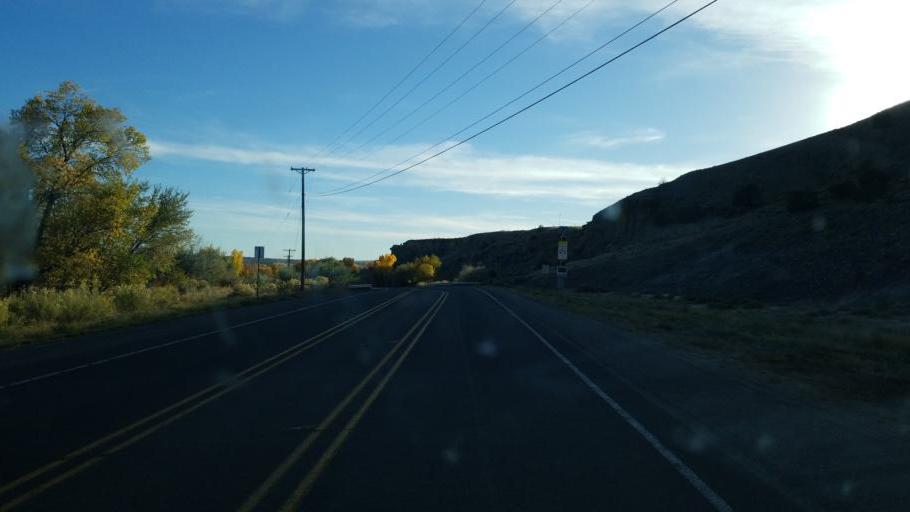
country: US
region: New Mexico
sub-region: San Juan County
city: Bloomfield
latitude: 36.7200
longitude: -107.8341
